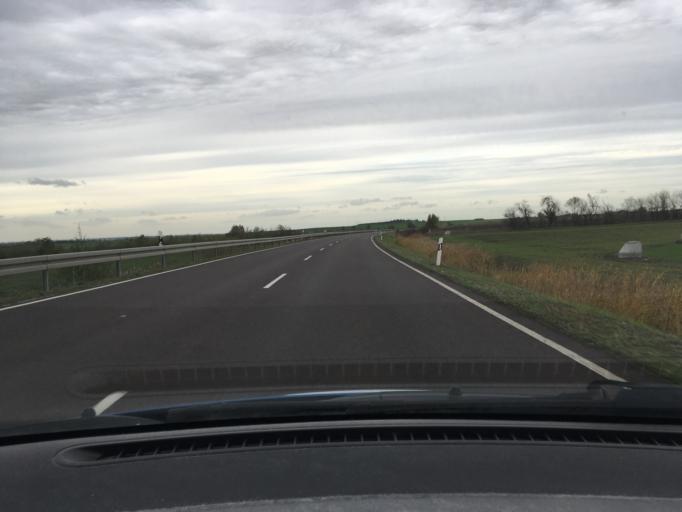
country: DE
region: Saxony-Anhalt
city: Leitzkau
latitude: 52.0526
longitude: 11.9431
